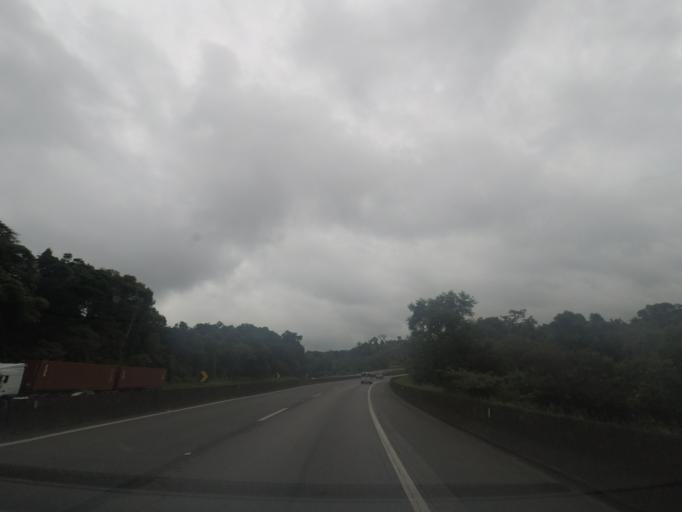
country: BR
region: Sao Paulo
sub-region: Cajati
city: Cajati
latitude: -24.9721
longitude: -48.3997
